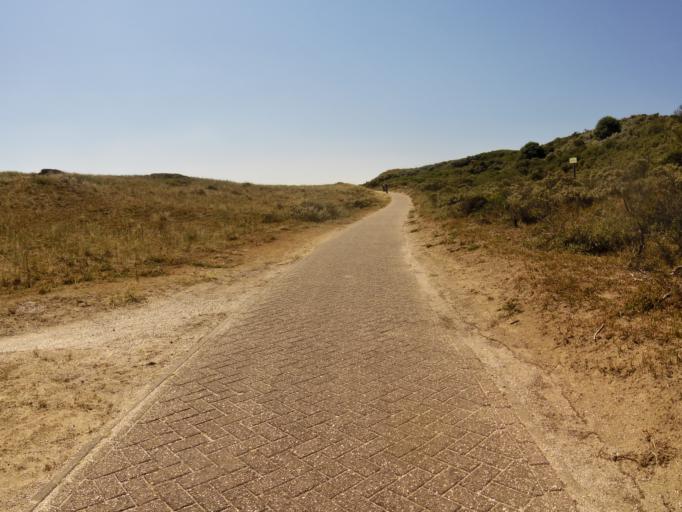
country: NL
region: North Holland
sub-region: Gemeente Zandvoort
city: Zandvoort
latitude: 52.4224
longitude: 4.5574
